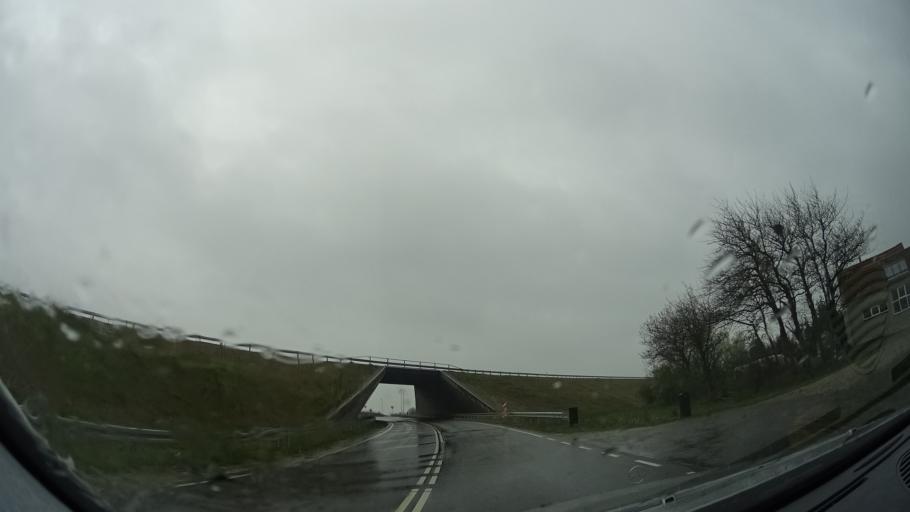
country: DK
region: Zealand
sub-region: Odsherred Kommune
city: Asnaes
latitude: 55.8164
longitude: 11.5826
